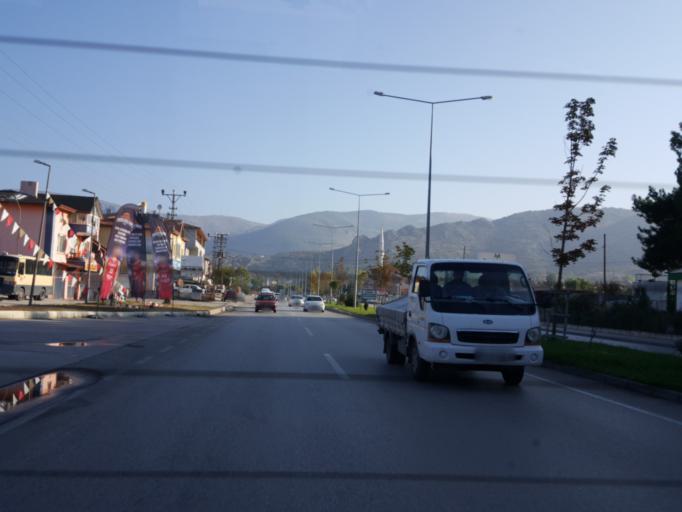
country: TR
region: Amasya
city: Amasya
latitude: 40.5999
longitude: 35.8080
